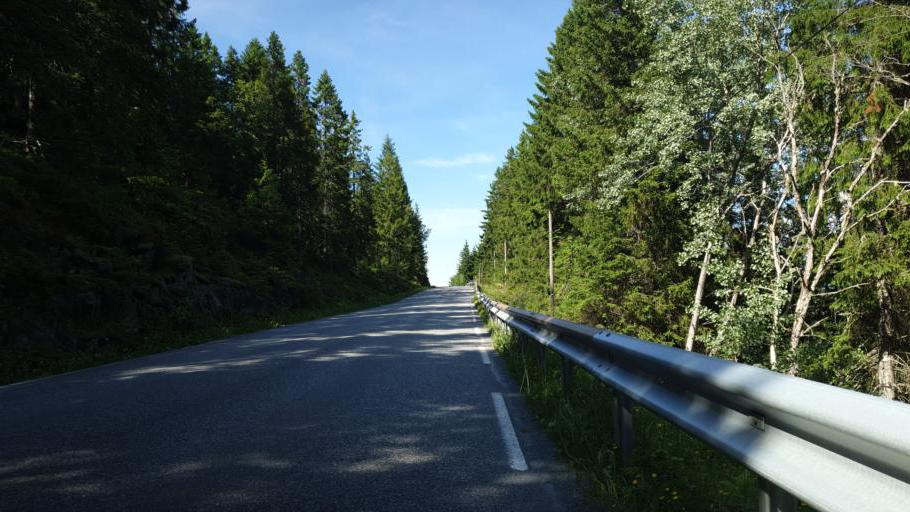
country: NO
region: Nord-Trondelag
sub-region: Leksvik
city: Leksvik
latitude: 63.6545
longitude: 10.6085
